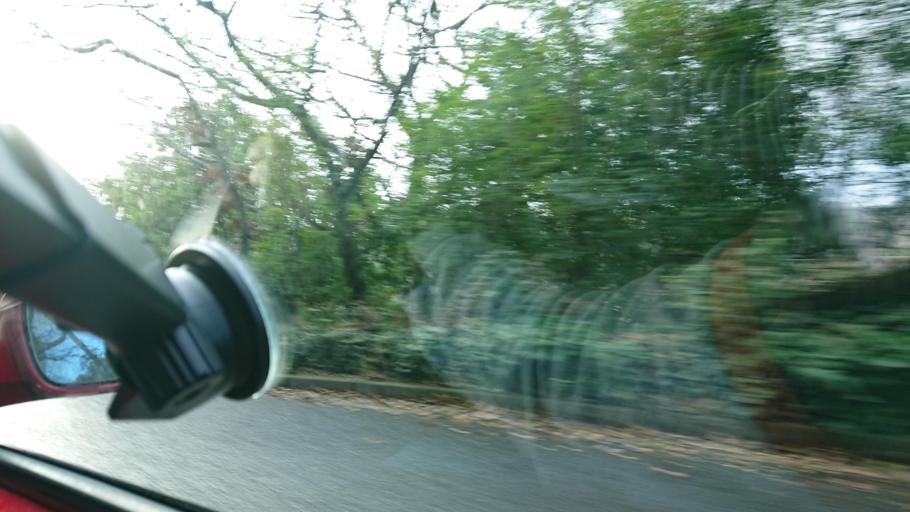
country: GB
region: England
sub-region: Cornwall
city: Looe
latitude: 50.3630
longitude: -4.4557
